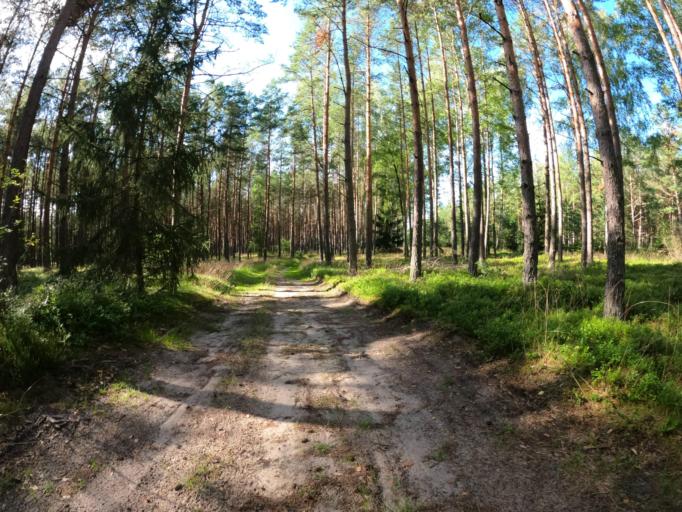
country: PL
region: West Pomeranian Voivodeship
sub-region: Powiat bialogardzki
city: Tychowo
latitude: 54.0496
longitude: 16.3093
